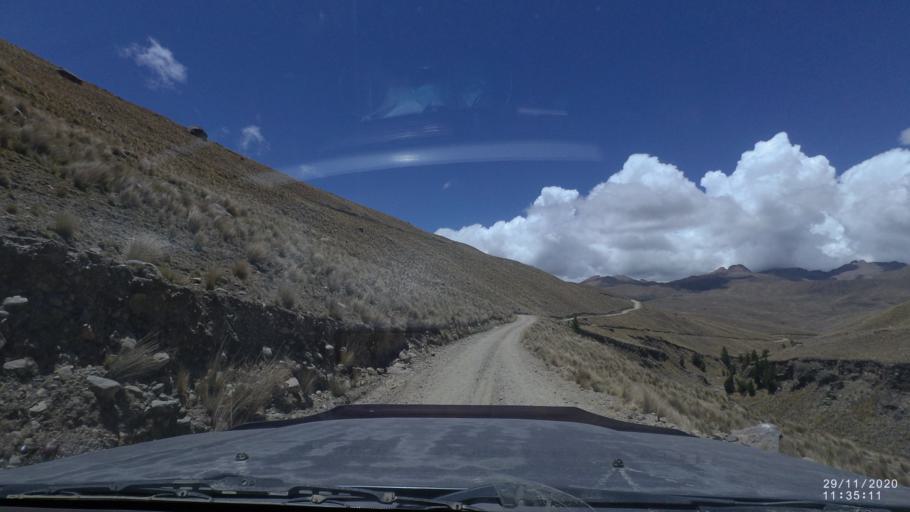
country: BO
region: Cochabamba
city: Cochabamba
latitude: -17.1919
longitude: -66.2231
